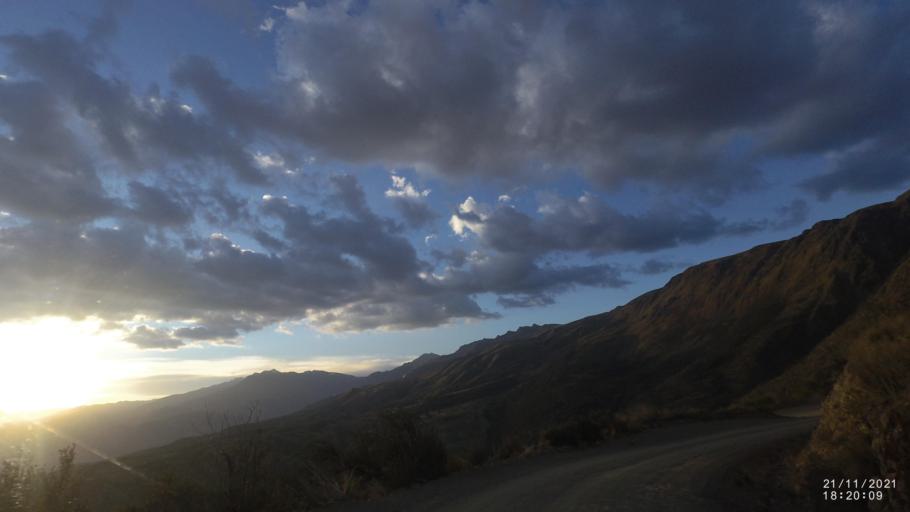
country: BO
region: Cochabamba
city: Cochabamba
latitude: -17.2934
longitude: -66.2200
